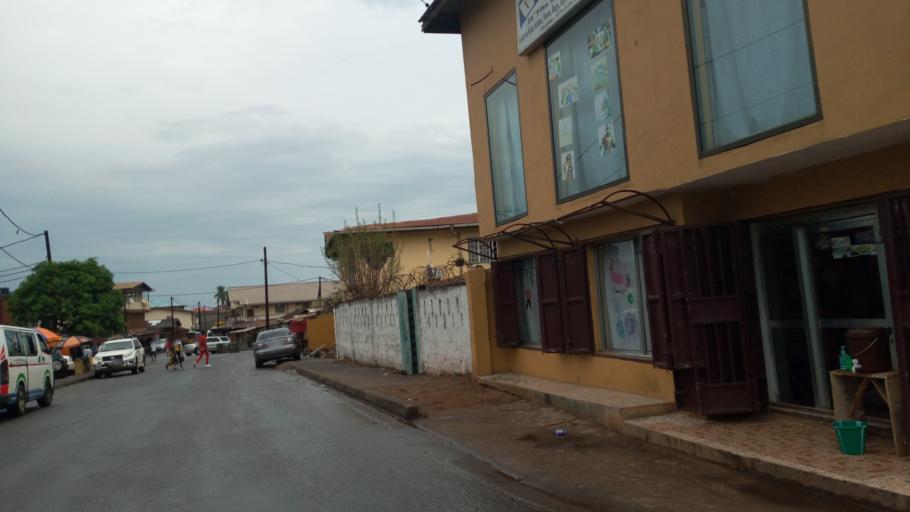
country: SL
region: Western Area
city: Freetown
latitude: 8.4733
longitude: -13.2402
